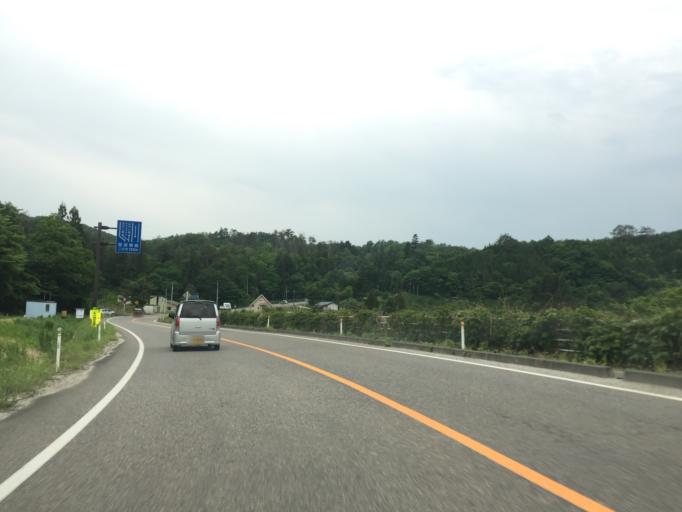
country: JP
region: Fukushima
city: Namie
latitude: 37.4331
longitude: 140.8095
